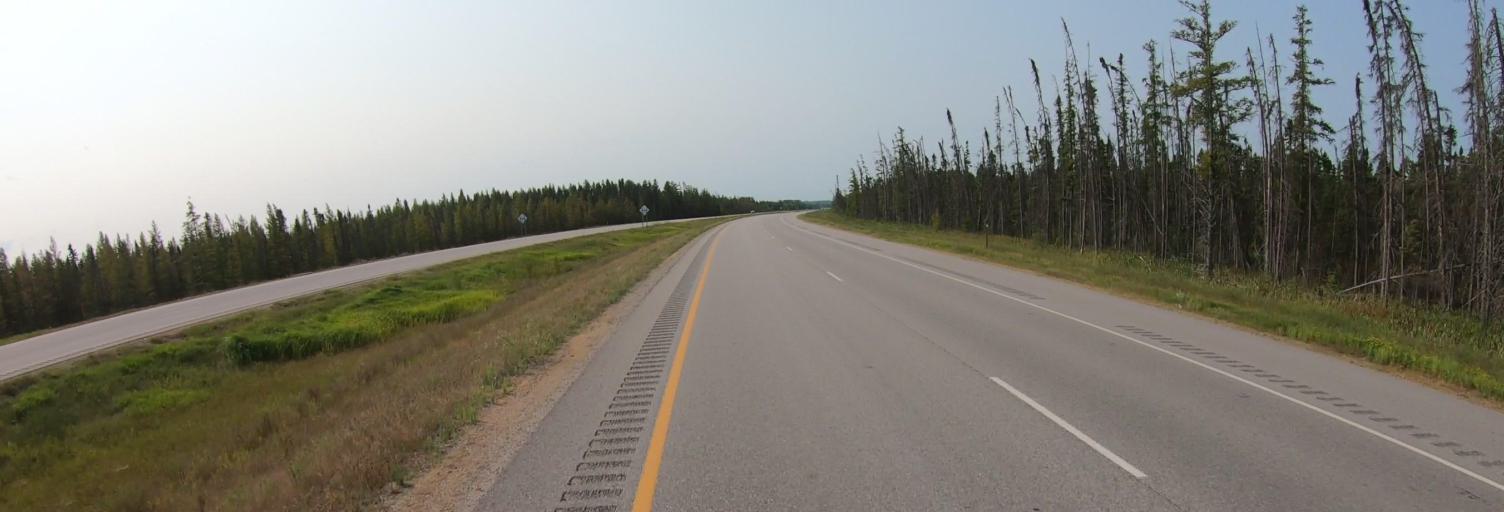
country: US
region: Minnesota
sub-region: Saint Louis County
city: Mountain Iron
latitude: 47.8369
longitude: -92.6750
